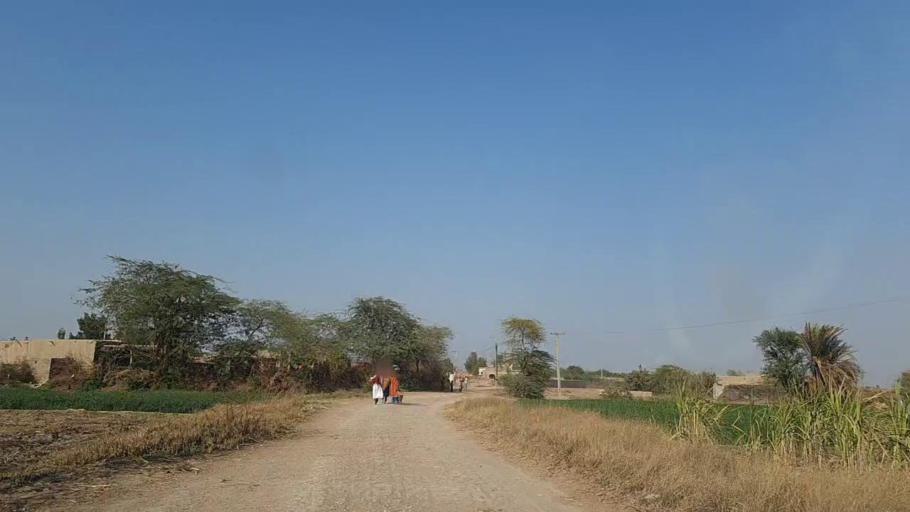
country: PK
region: Sindh
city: Daur
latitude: 26.4613
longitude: 68.3031
